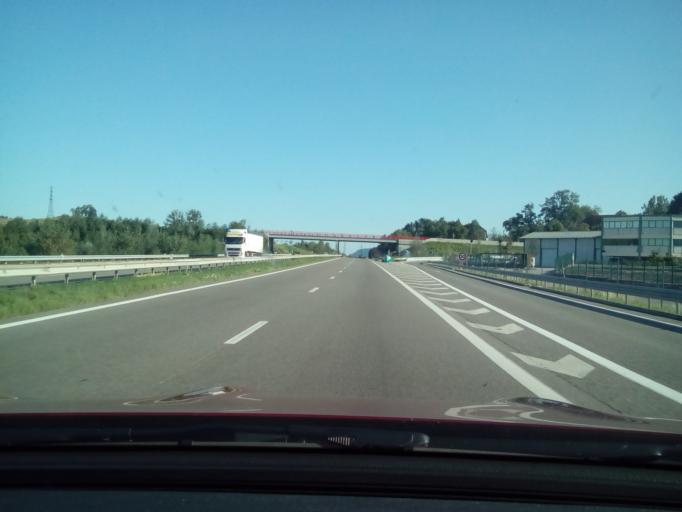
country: FR
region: Rhone-Alpes
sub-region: Departement de la Haute-Savoie
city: Viuz-la-Chiesaz
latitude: 45.8465
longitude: 6.0570
